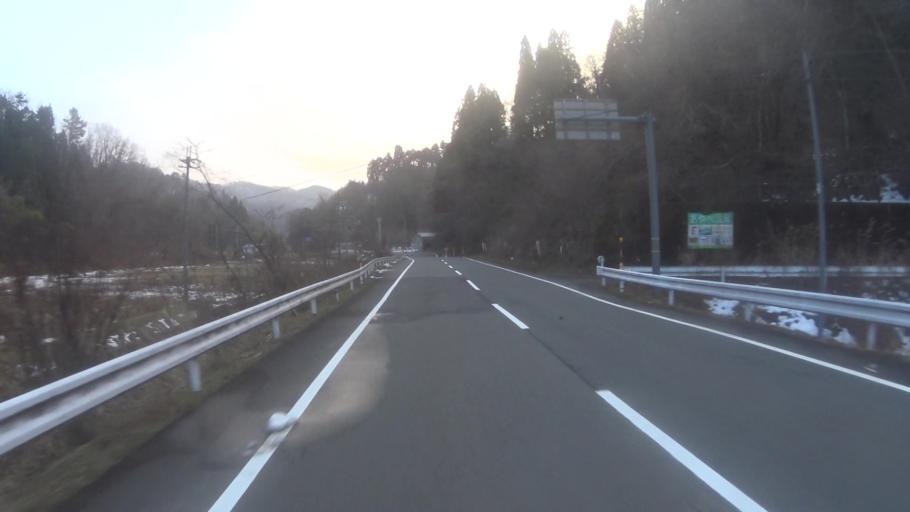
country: JP
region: Kyoto
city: Maizuru
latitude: 35.4343
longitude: 135.4787
